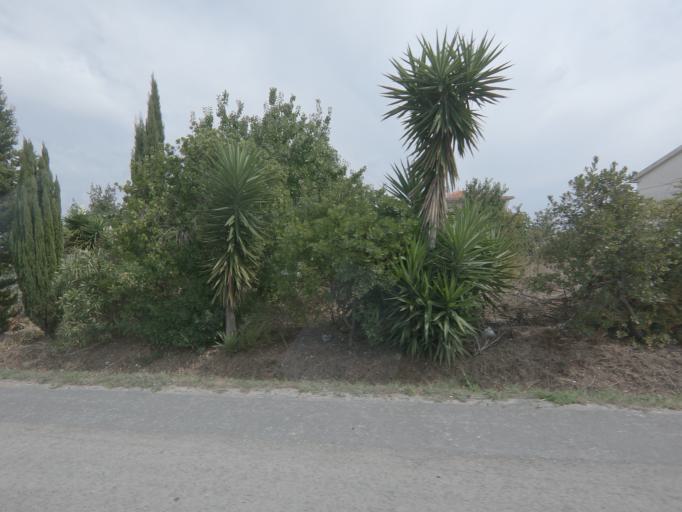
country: PT
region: Leiria
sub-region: Pombal
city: Pombal
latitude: 39.8816
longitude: -8.6763
